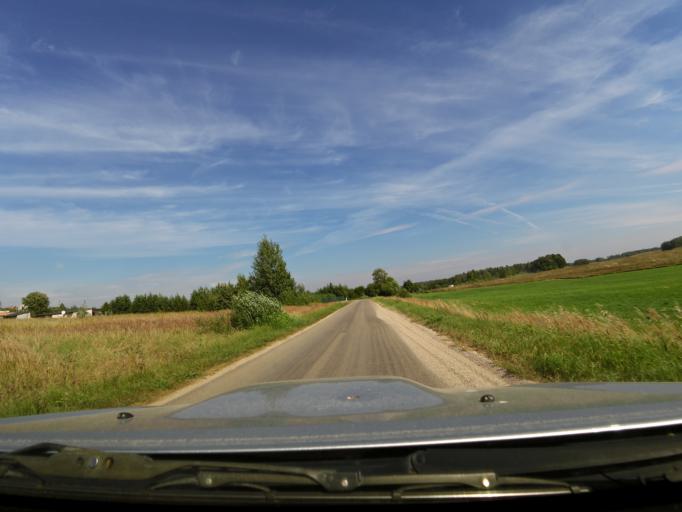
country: LT
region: Vilnius County
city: Pasilaiciai
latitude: 54.8334
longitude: 25.1598
